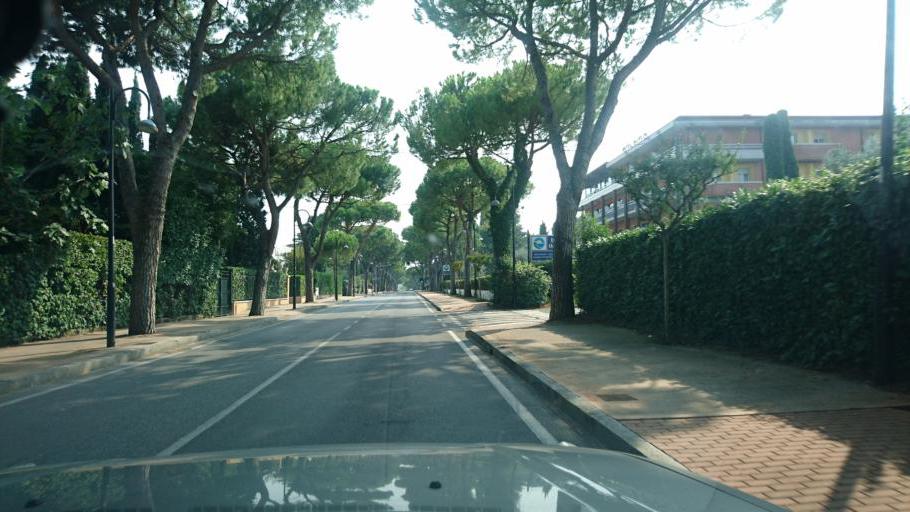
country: IT
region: Lombardy
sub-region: Provincia di Brescia
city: Desenzano del Garda
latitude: 45.4822
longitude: 10.5383
